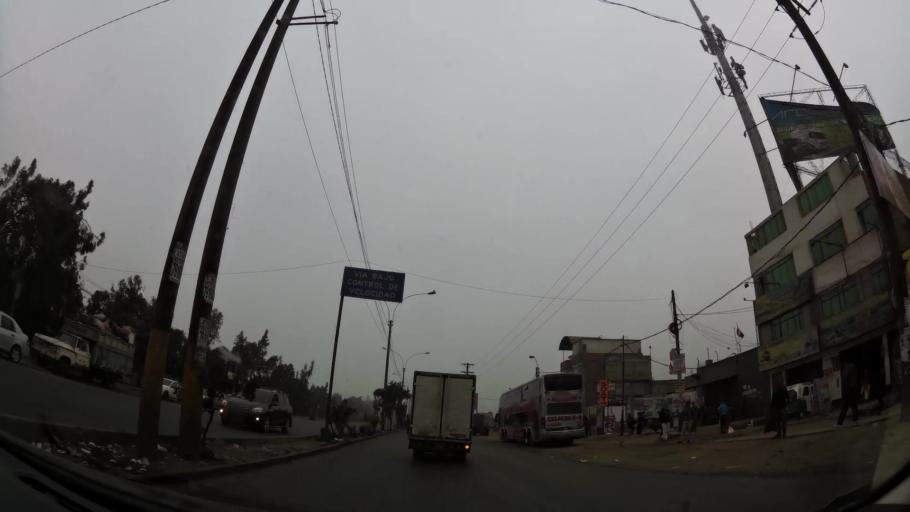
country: PE
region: Lima
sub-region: Lima
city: Santa Maria
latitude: -11.9995
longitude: -76.8382
